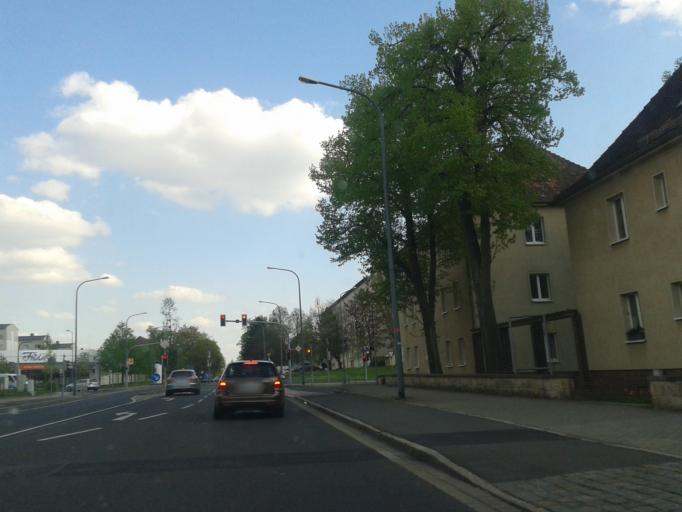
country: DE
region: Saxony
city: Albertstadt
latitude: 51.1192
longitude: 13.7657
